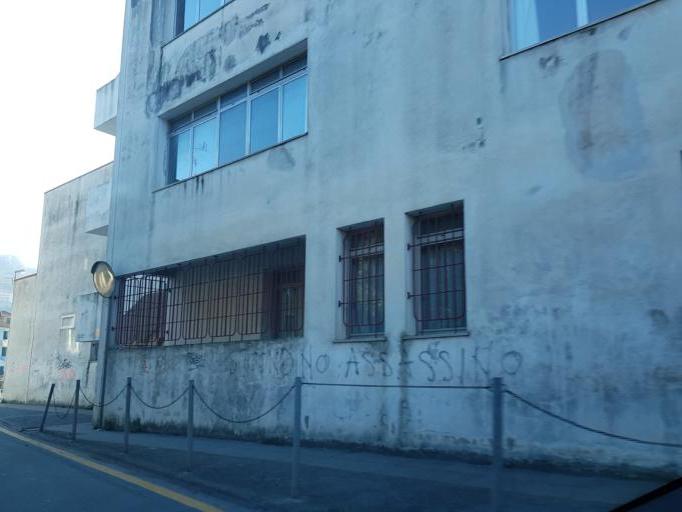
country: IT
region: Liguria
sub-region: Provincia di Genova
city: Santa Marta
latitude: 44.4975
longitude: 8.9013
